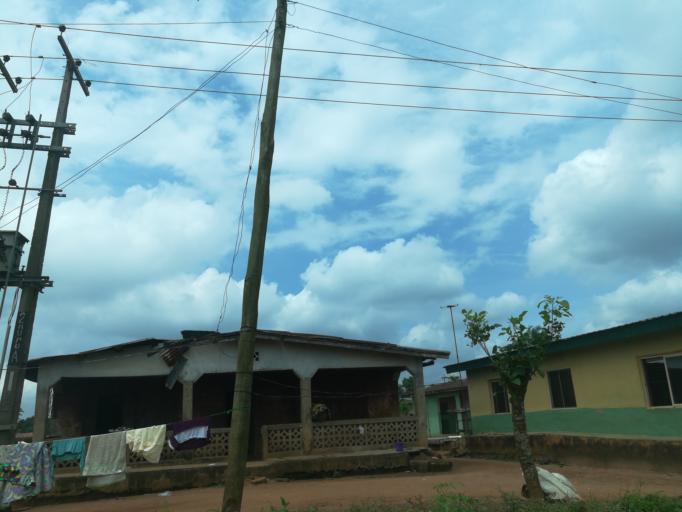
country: NG
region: Lagos
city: Ejirin
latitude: 6.6416
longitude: 3.7115
